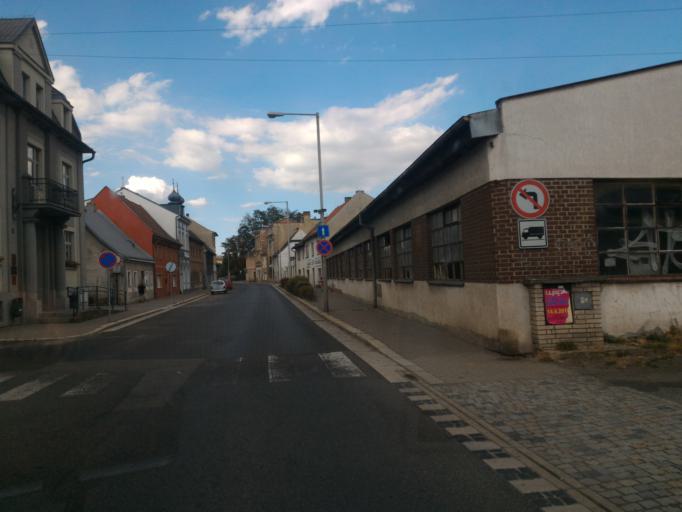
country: CZ
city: Mimon
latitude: 50.6563
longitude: 14.7255
